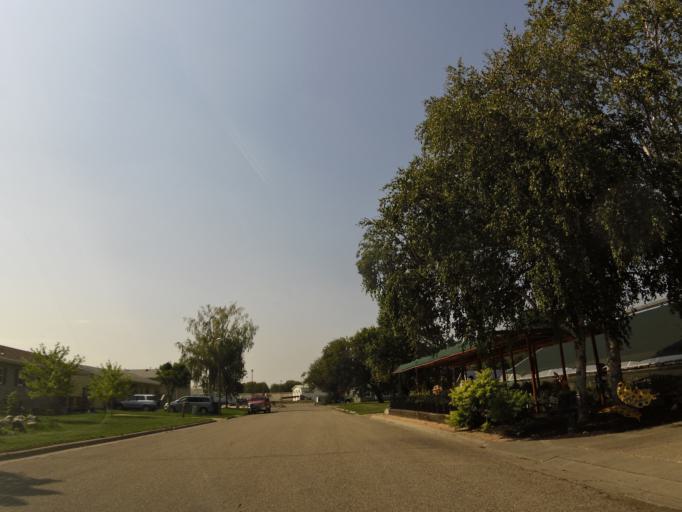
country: US
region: North Dakota
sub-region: Walsh County
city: Grafton
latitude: 48.4145
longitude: -97.4043
